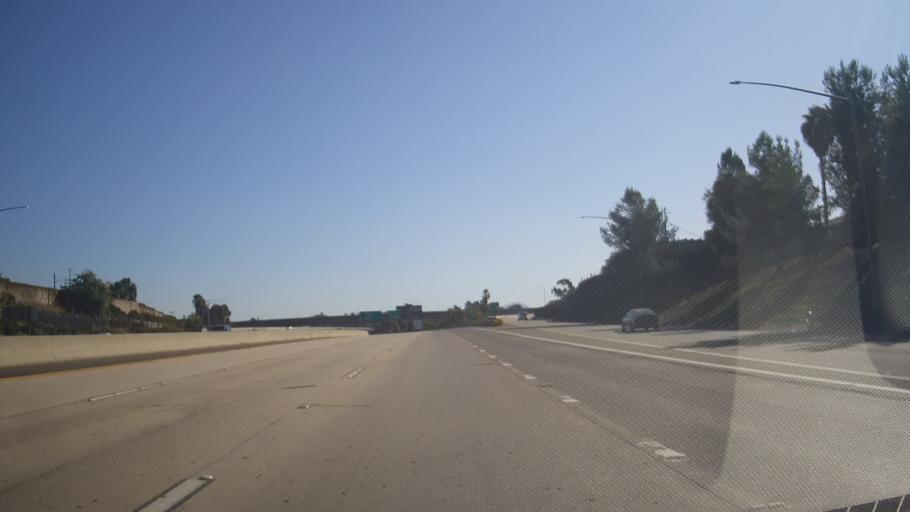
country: US
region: California
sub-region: San Diego County
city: Lemon Grove
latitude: 32.7464
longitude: -117.0232
